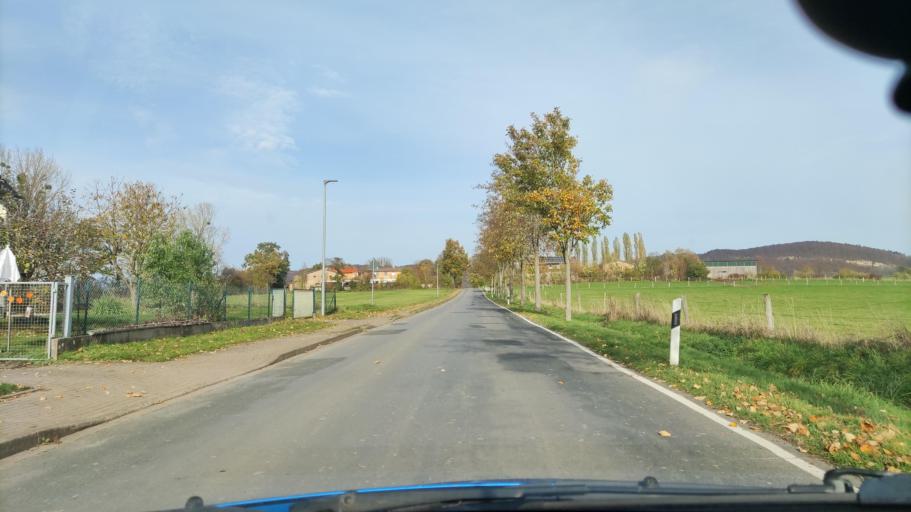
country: DE
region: Lower Saxony
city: Holzen
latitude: 51.9202
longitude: 9.6641
